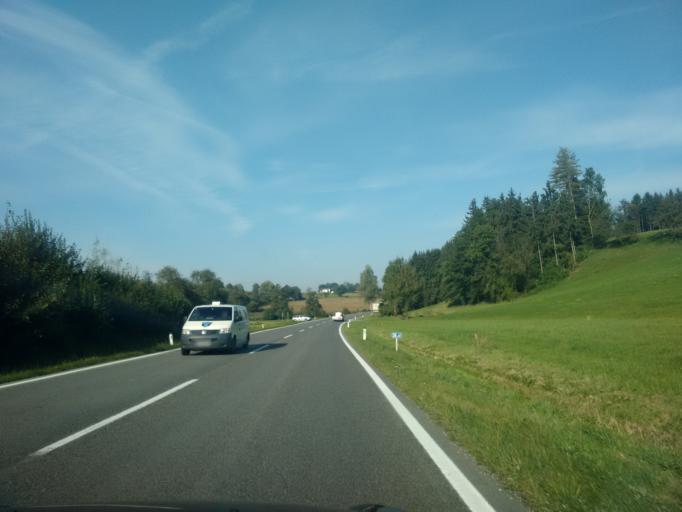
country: AT
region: Upper Austria
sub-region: Politischer Bezirk Vocklabruck
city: Wolfsegg am Hausruck
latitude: 48.2904
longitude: 13.6561
